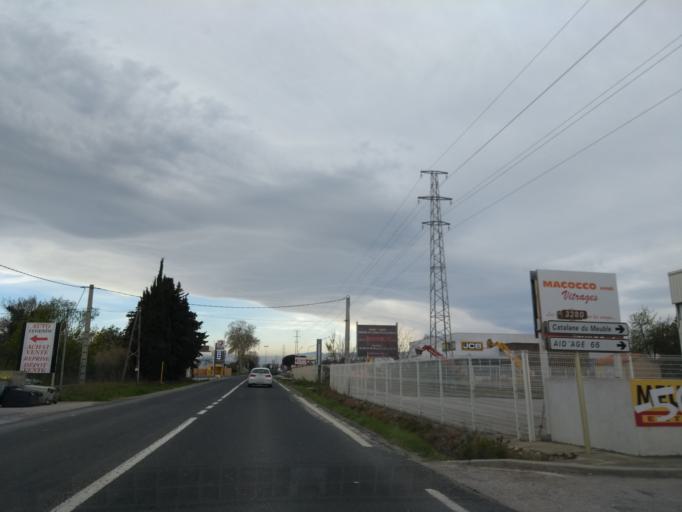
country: FR
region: Languedoc-Roussillon
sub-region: Departement des Pyrenees-Orientales
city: Baho
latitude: 42.6907
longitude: 2.8369
